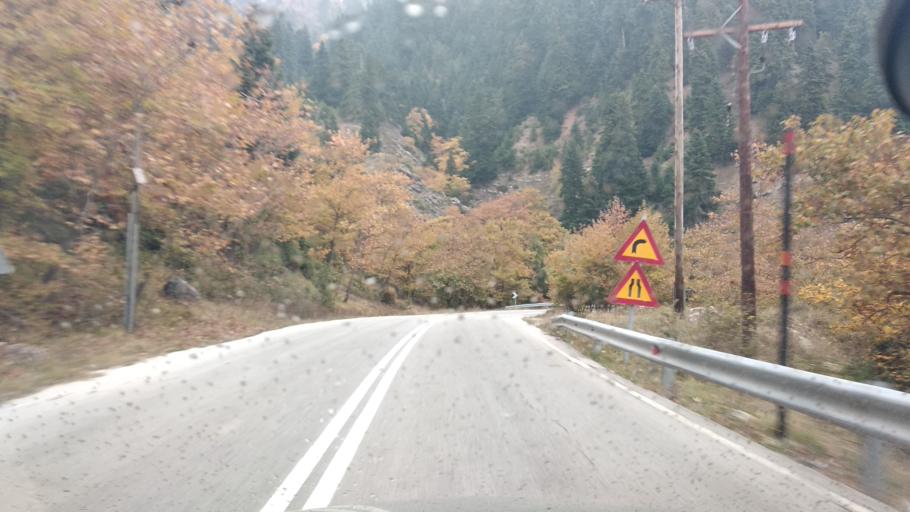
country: GR
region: Thessaly
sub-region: Trikala
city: Pyli
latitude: 39.5221
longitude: 21.5219
